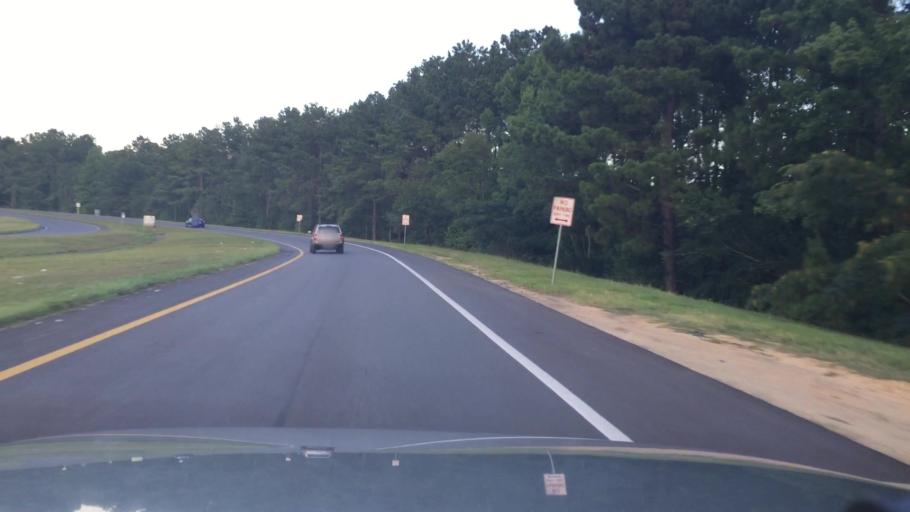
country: US
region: South Carolina
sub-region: Richland County
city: Forest Acres
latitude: 33.9489
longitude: -80.9732
